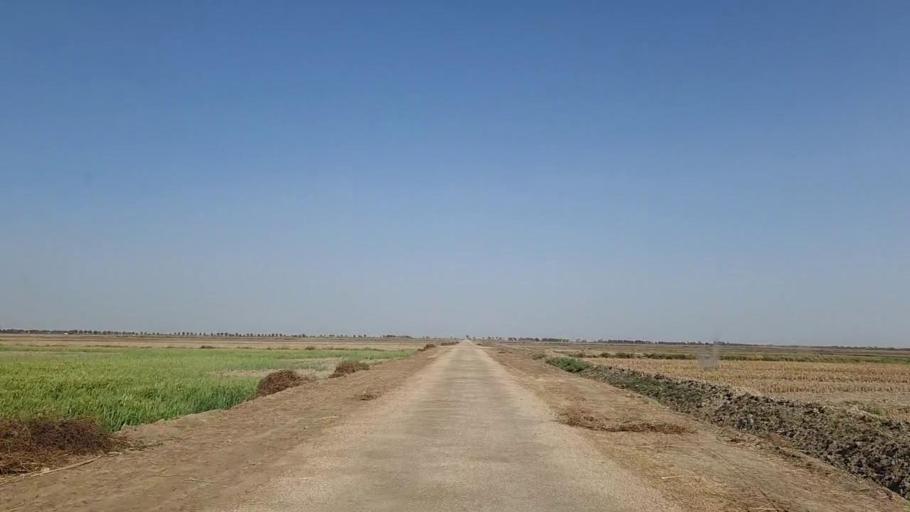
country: PK
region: Sindh
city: Jati
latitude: 24.5135
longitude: 68.1939
